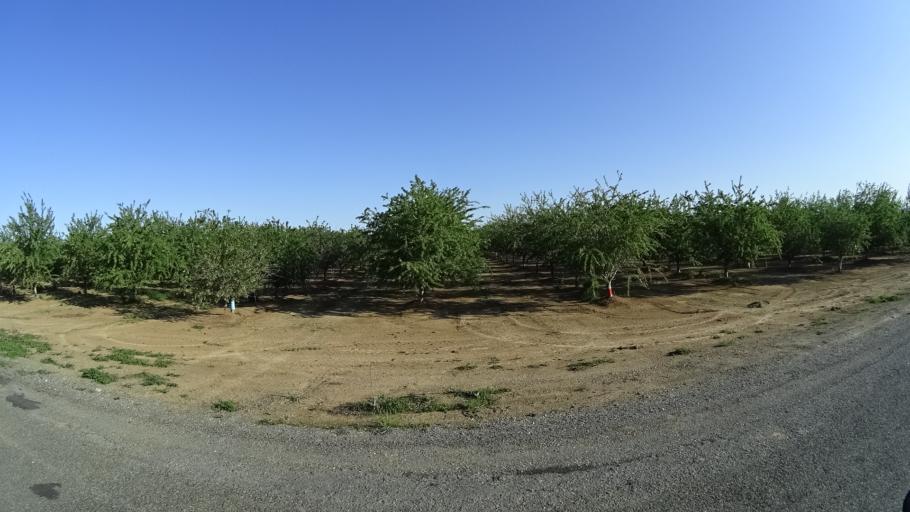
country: US
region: California
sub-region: Glenn County
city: Orland
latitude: 39.7976
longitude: -122.1348
